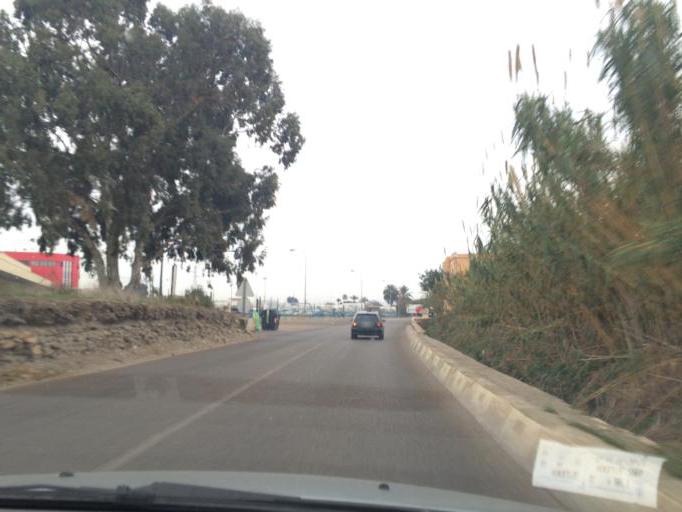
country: ES
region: Andalusia
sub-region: Provincia de Almeria
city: Almeria
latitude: 36.8403
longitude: -2.4238
